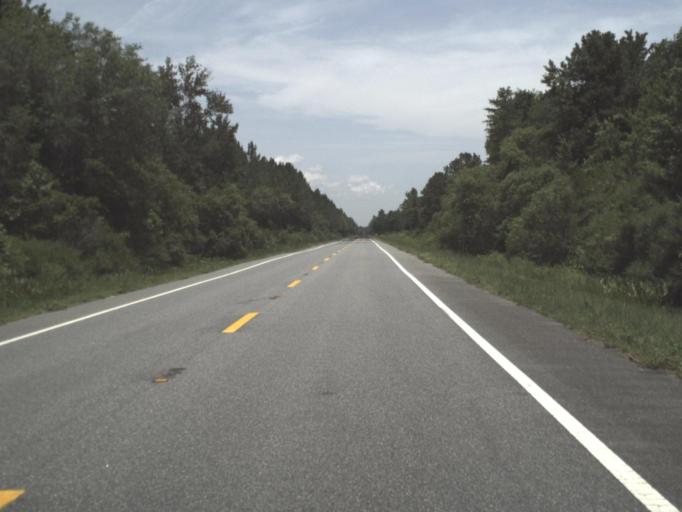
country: US
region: Florida
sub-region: Taylor County
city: Steinhatchee
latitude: 29.8586
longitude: -83.3088
